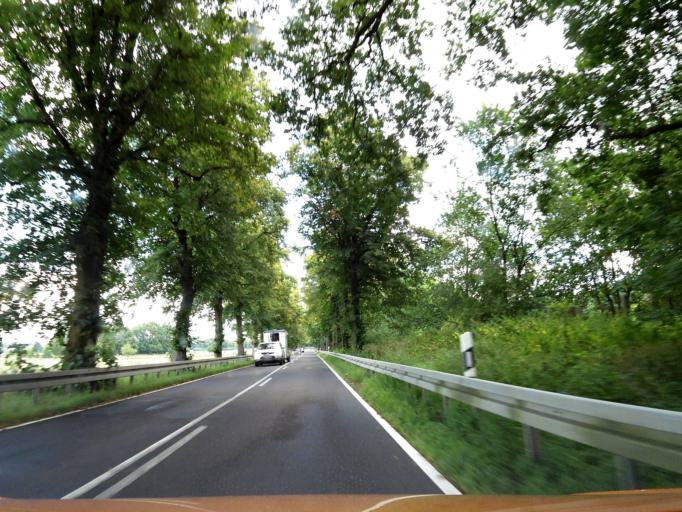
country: DE
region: Brandenburg
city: Potsdam
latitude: 52.4611
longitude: 12.9962
